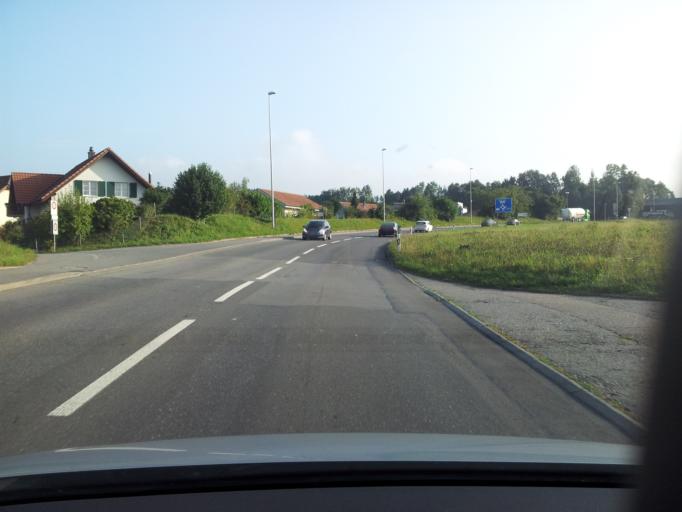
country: CH
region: Lucerne
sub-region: Sursee District
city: Sempach
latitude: 47.1347
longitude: 8.1963
